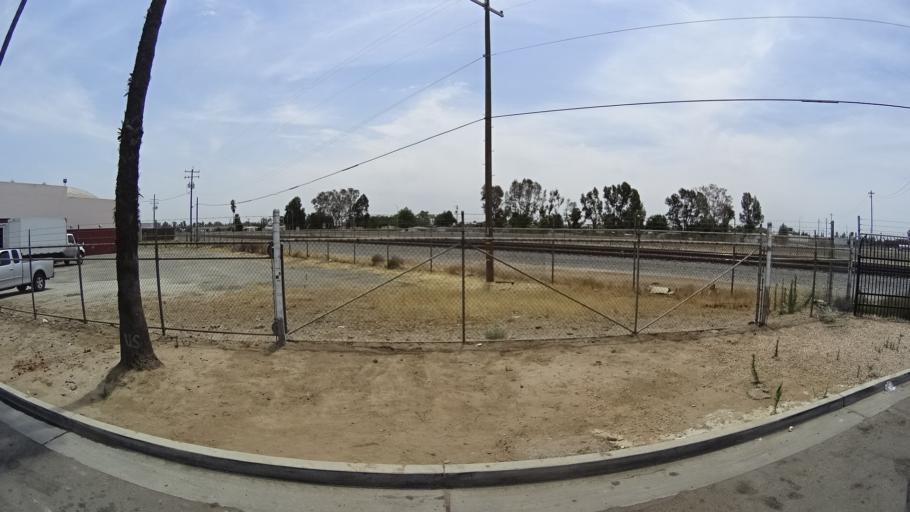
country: US
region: California
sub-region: Fresno County
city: West Park
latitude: 36.7702
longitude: -119.8347
